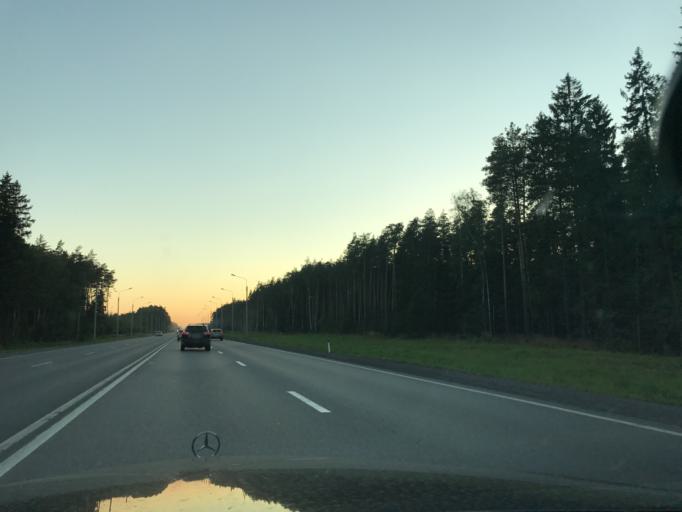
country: RU
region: Vladimir
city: Pokrov
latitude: 55.9248
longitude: 39.2728
